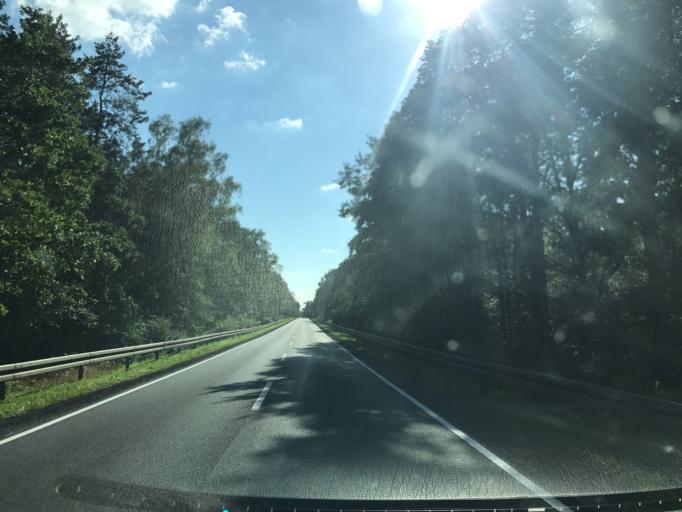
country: PL
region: Kujawsko-Pomorskie
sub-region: Wloclawek
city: Wloclawek
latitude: 52.6291
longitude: 19.0047
